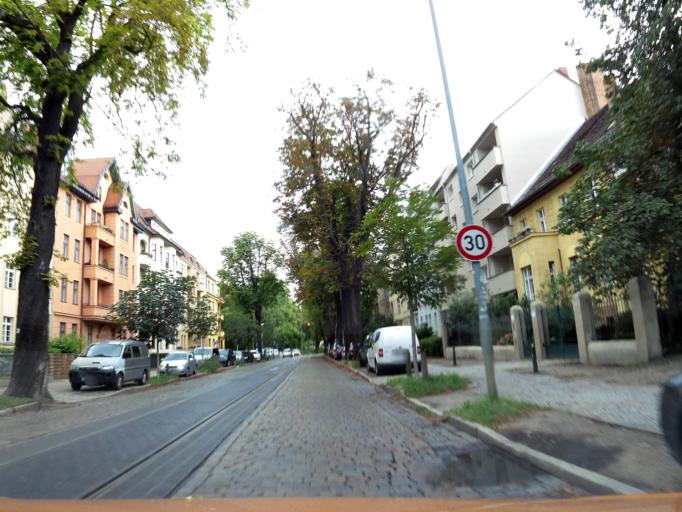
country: DE
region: Brandenburg
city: Potsdam
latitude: 52.3924
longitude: 13.0277
